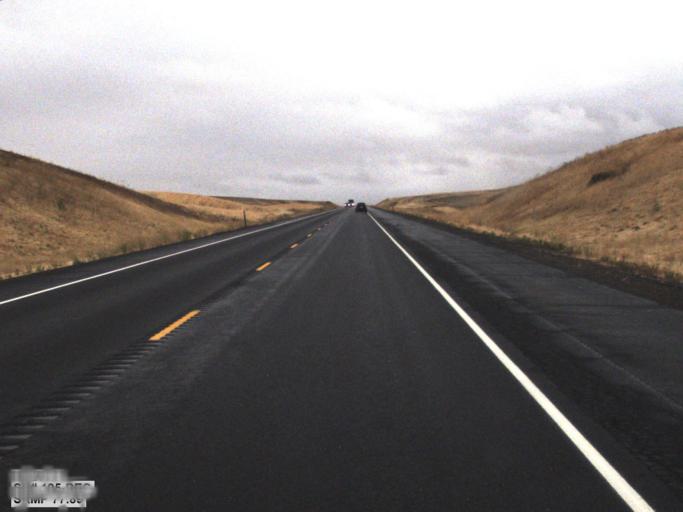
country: US
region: Washington
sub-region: Spokane County
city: Cheney
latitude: 47.4100
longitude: -117.3917
